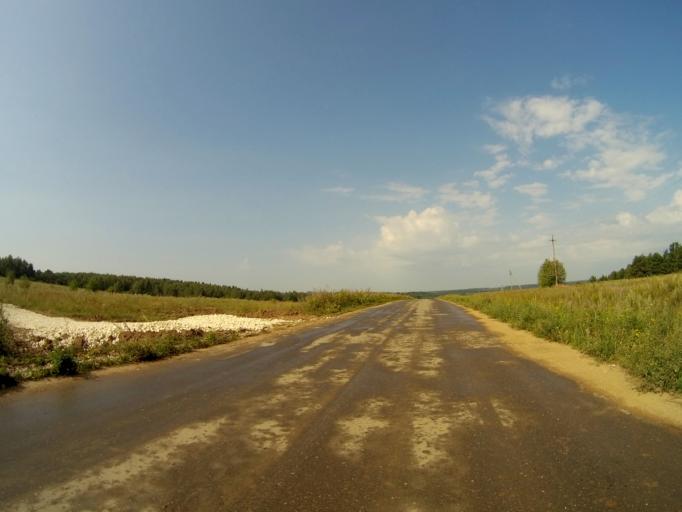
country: RU
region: Vladimir
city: Vladimir
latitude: 56.1309
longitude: 40.2894
